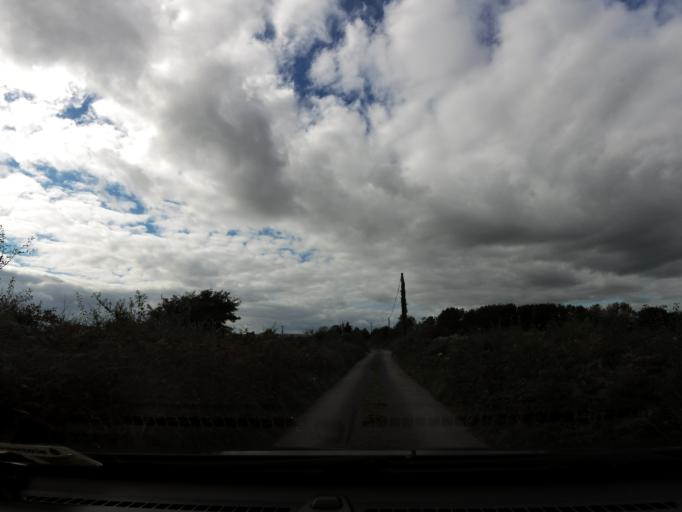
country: IE
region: Connaught
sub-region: County Galway
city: Moycullen
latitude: 53.3189
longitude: -9.1388
